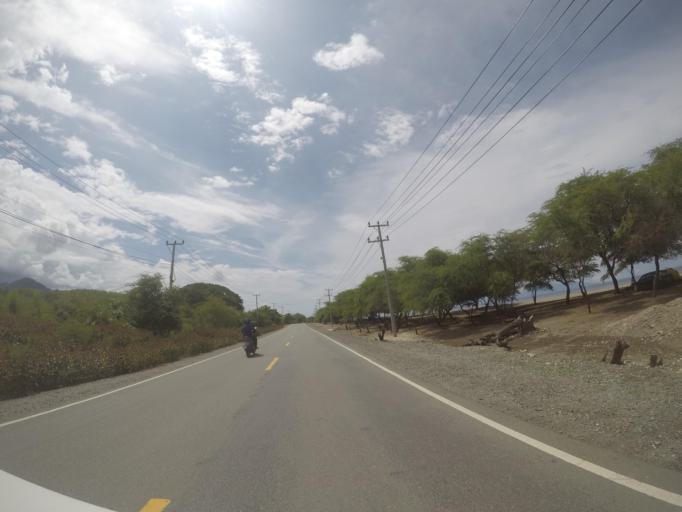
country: TL
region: Liquica
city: Liquica
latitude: -8.5648
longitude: 125.3980
